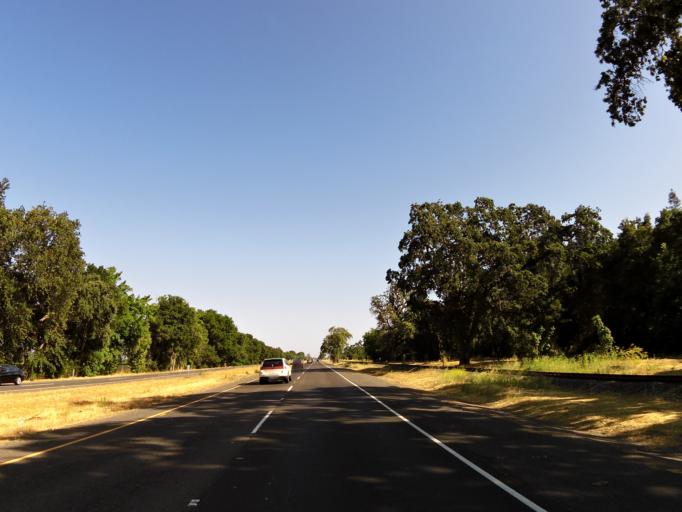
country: US
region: California
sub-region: Napa County
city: Yountville
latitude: 38.3592
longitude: -122.3348
